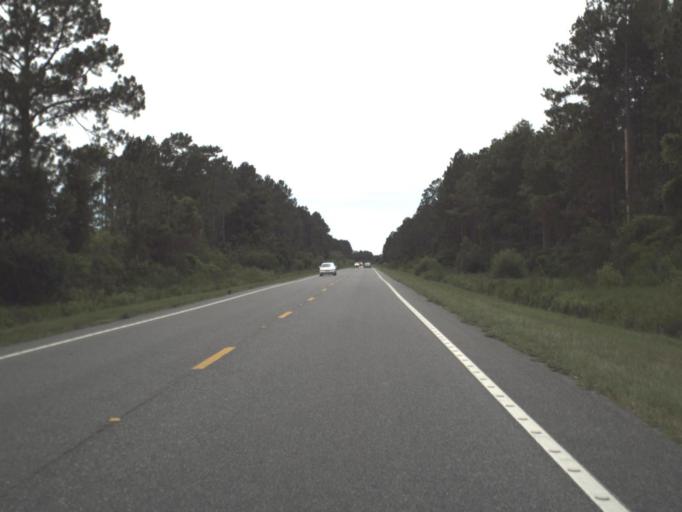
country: US
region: Florida
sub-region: Taylor County
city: Perry
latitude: 30.1242
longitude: -83.3899
